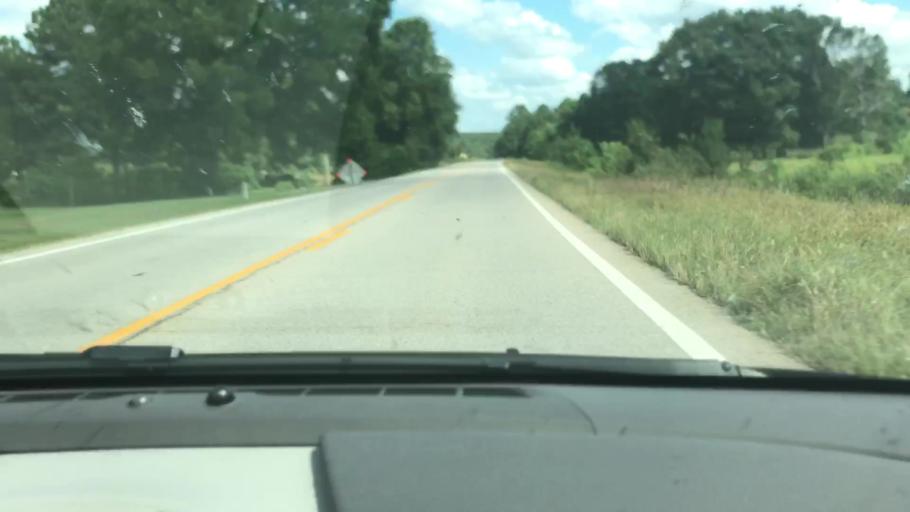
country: US
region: Georgia
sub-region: Troup County
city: West Point
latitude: 32.8875
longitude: -85.0337
